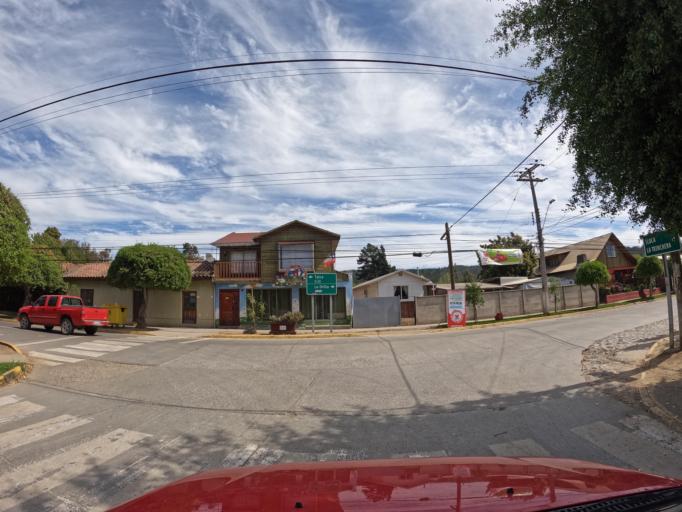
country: CL
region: Maule
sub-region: Provincia de Talca
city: Constitucion
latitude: -35.0906
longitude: -72.0220
